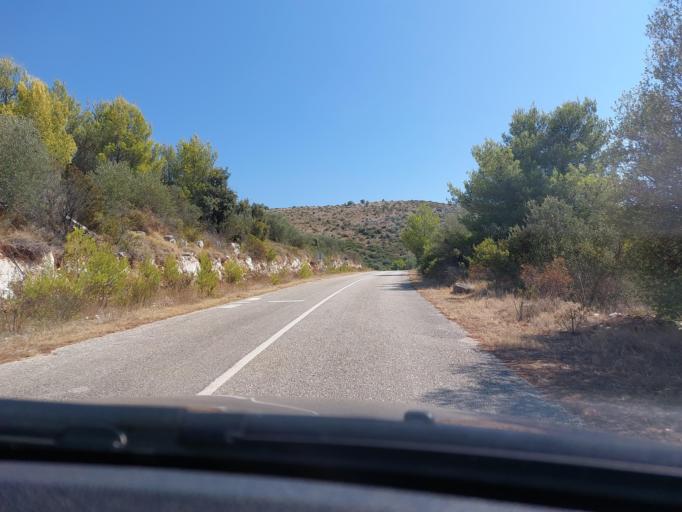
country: HR
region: Dubrovacko-Neretvanska
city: Smokvica
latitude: 42.7514
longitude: 16.8782
